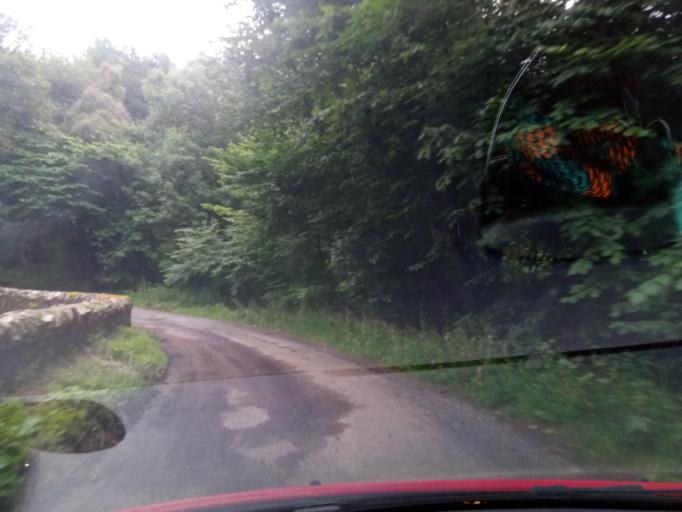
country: GB
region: Scotland
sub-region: Fife
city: Pathhead
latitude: 55.7423
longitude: -2.9237
